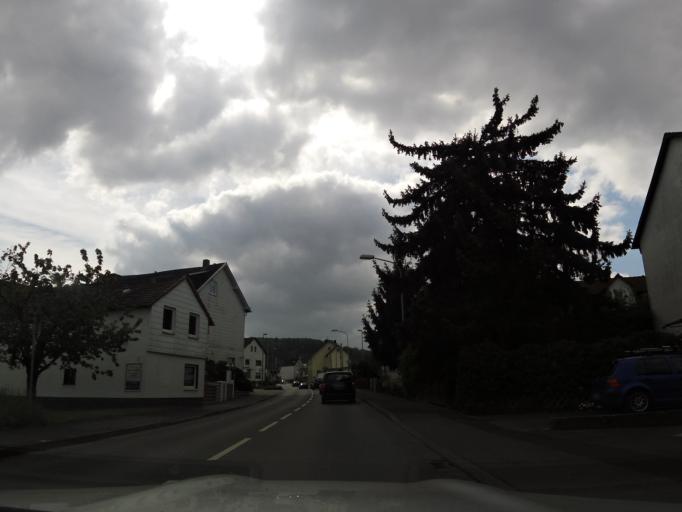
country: DE
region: Hesse
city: Albshausen
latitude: 50.5463
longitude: 8.4333
